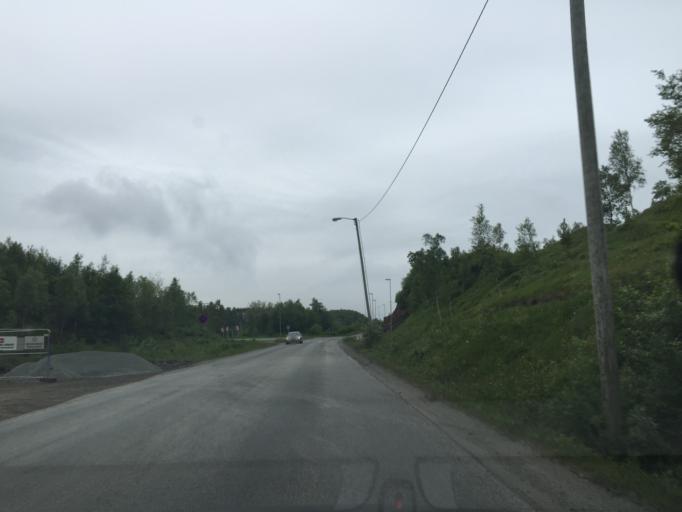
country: NO
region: Nordland
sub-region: Bodo
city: Lopsmarka
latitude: 67.2857
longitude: 14.5567
